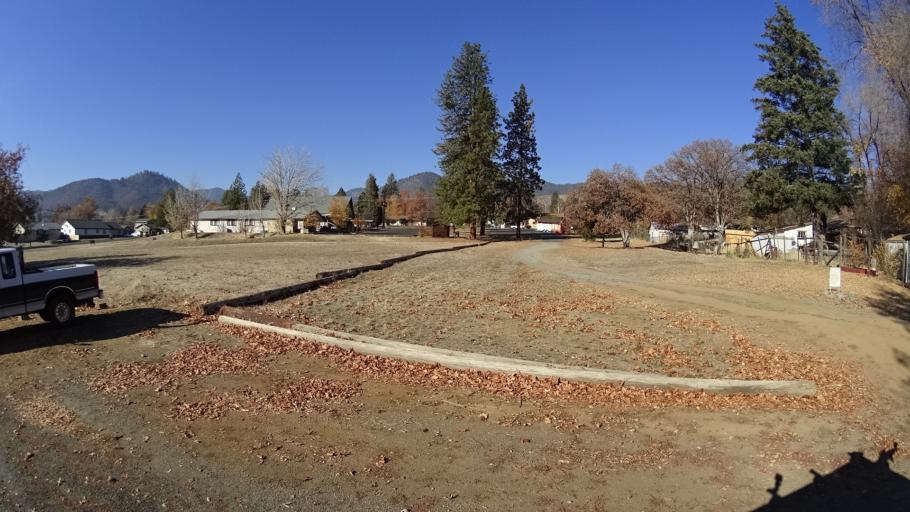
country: US
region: California
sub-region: Siskiyou County
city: Yreka
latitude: 41.7378
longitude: -122.6426
